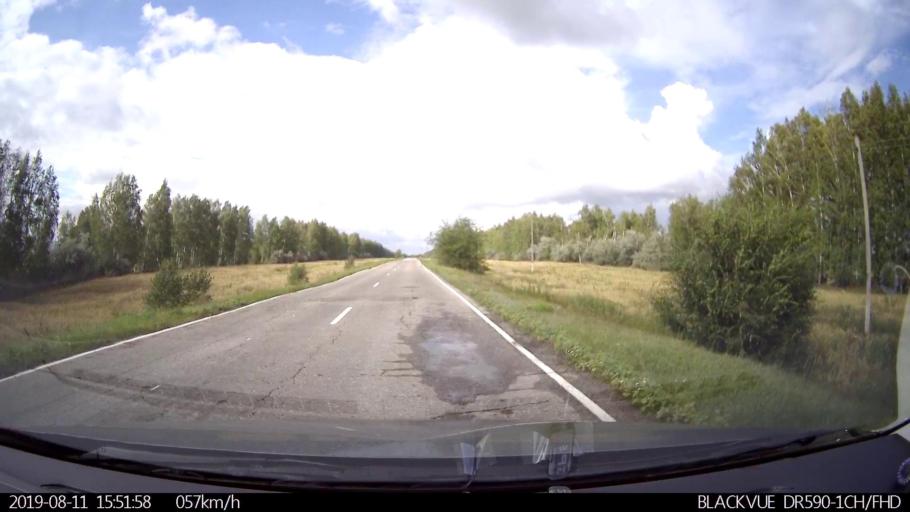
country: RU
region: Ulyanovsk
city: Ignatovka
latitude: 53.9230
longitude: 47.6562
